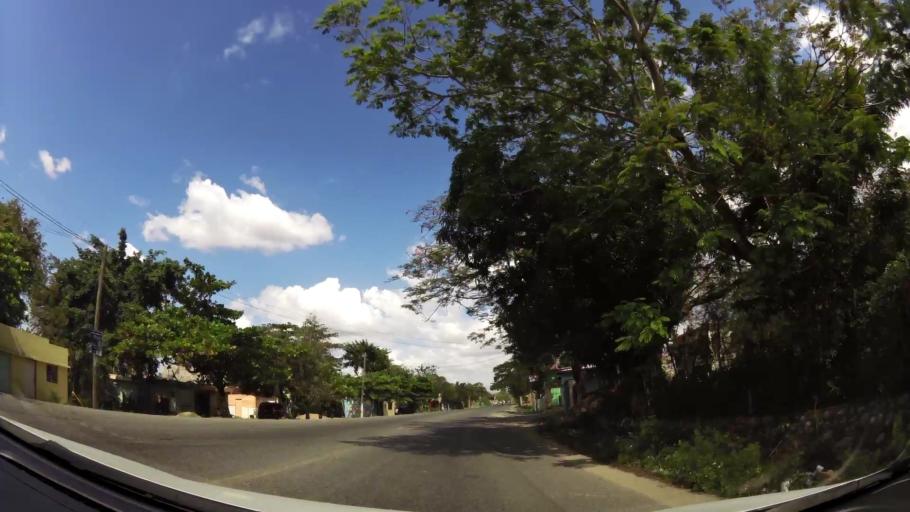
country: DO
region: San Cristobal
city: San Cristobal
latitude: 18.4265
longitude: -70.0668
